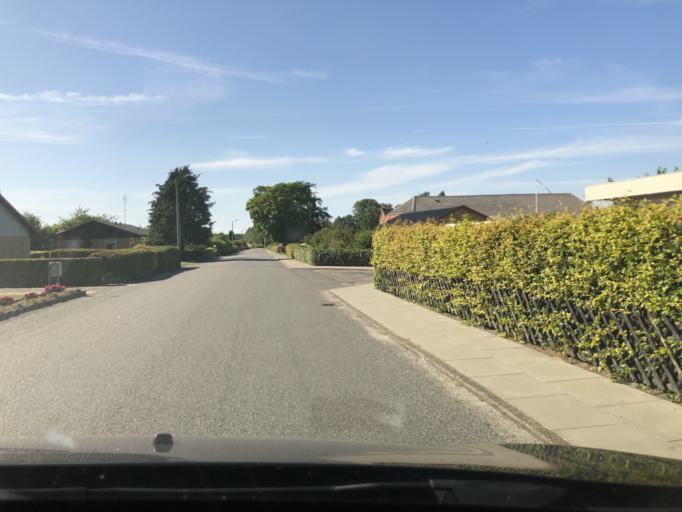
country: DK
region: South Denmark
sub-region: AEro Kommune
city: Marstal
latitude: 54.8601
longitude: 10.5120
